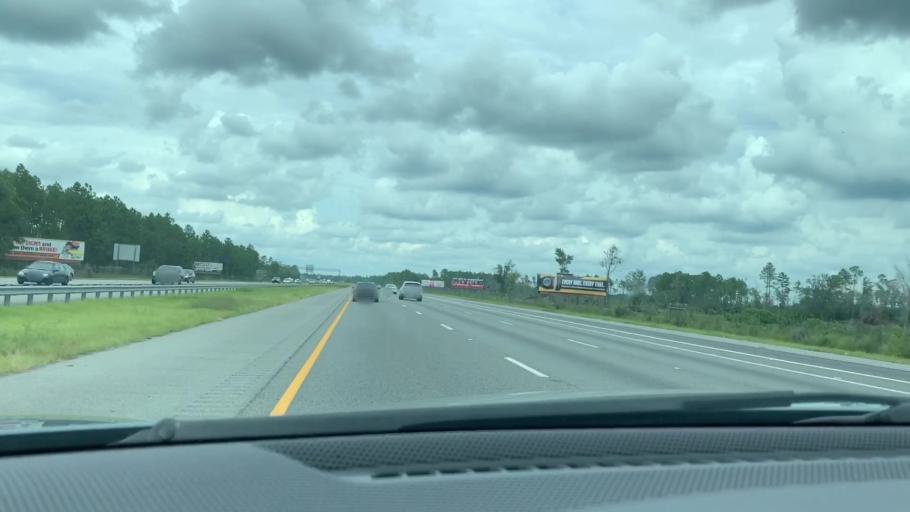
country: US
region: Georgia
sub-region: McIntosh County
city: Darien
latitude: 31.4028
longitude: -81.4468
